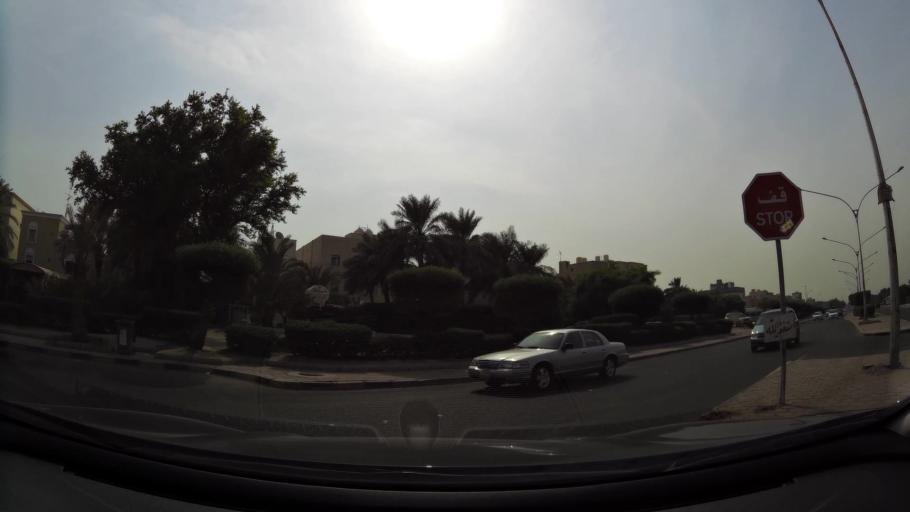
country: KW
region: Al Asimah
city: Ar Rabiyah
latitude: 29.2887
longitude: 47.9343
